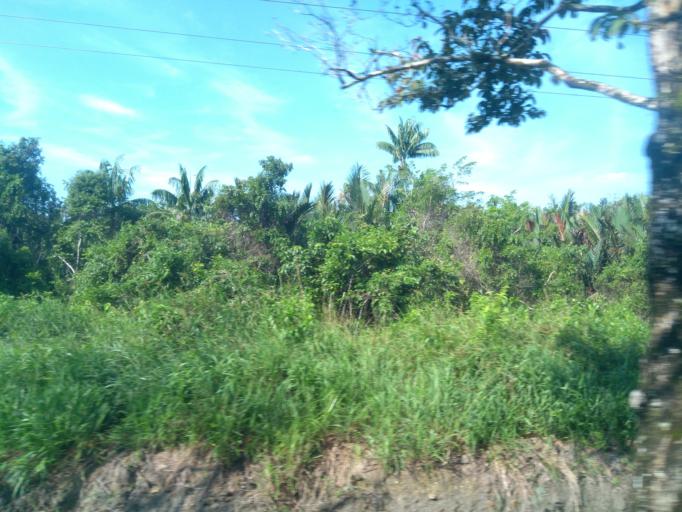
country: MY
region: Sarawak
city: Kuching
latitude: 1.6589
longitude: 110.4373
